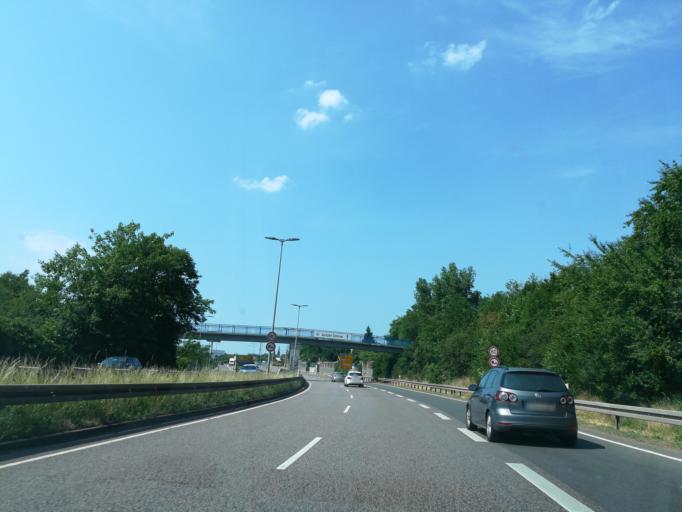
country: DE
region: Saxony-Anhalt
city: Magdeburg
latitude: 52.0993
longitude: 11.6057
